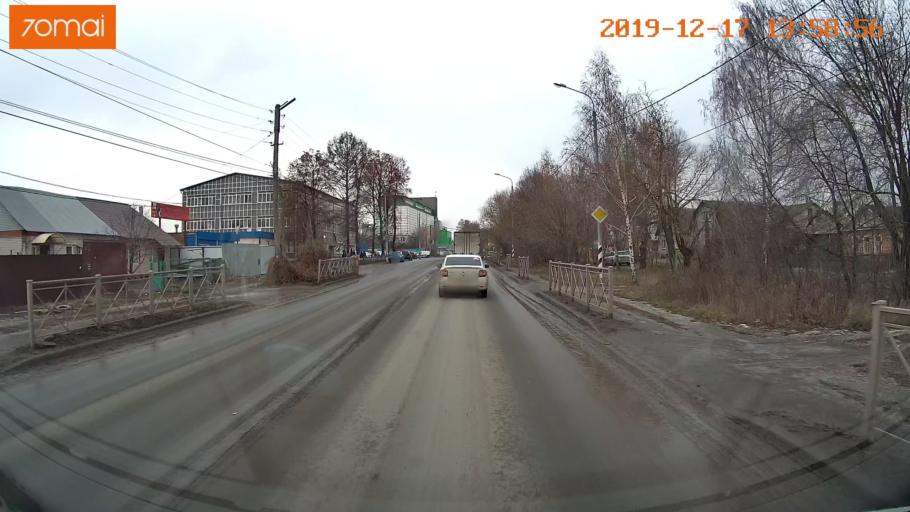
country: RU
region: Rjazan
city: Ryazan'
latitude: 54.6219
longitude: 39.6811
